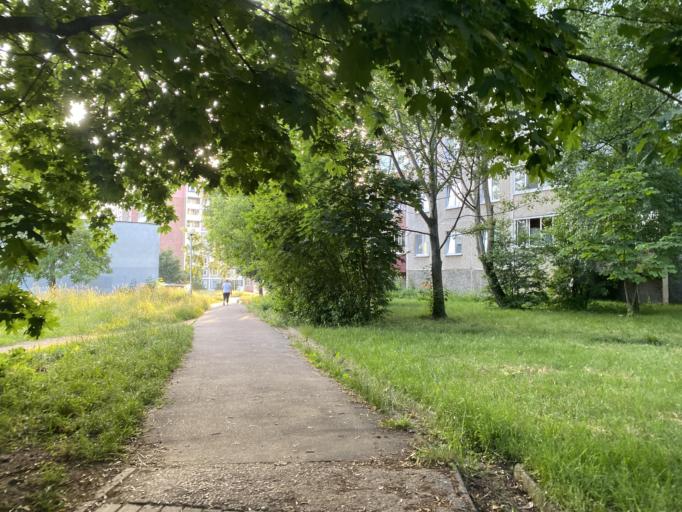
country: BY
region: Minsk
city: Bal'shavik
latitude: 53.9599
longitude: 27.6194
